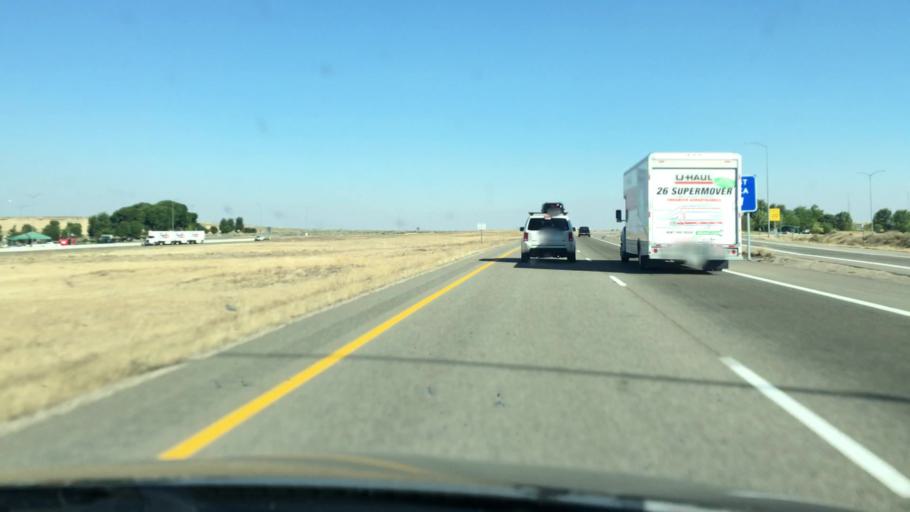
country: US
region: Idaho
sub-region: Ada County
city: Boise
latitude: 43.4799
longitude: -116.1098
